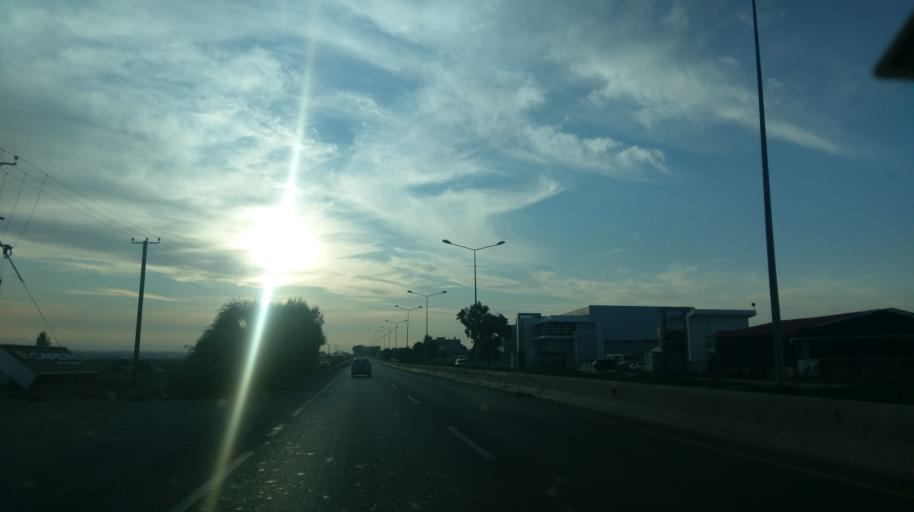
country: CY
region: Lefkosia
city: Nicosia
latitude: 35.2159
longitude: 33.4539
